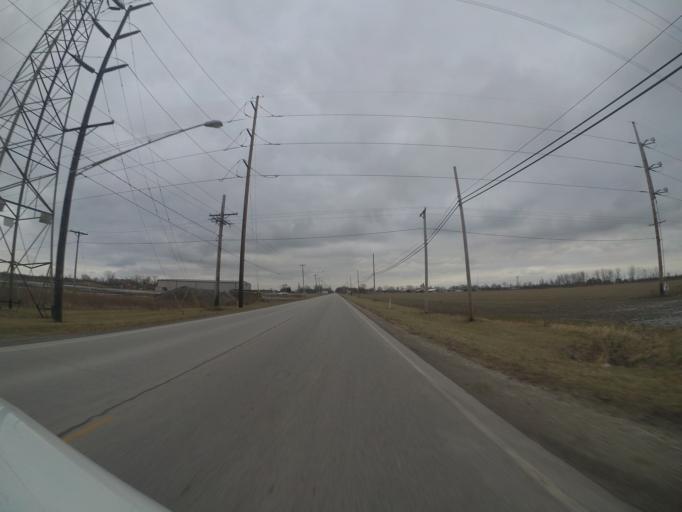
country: US
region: Ohio
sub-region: Wood County
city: Walbridge
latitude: 41.5927
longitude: -83.5127
